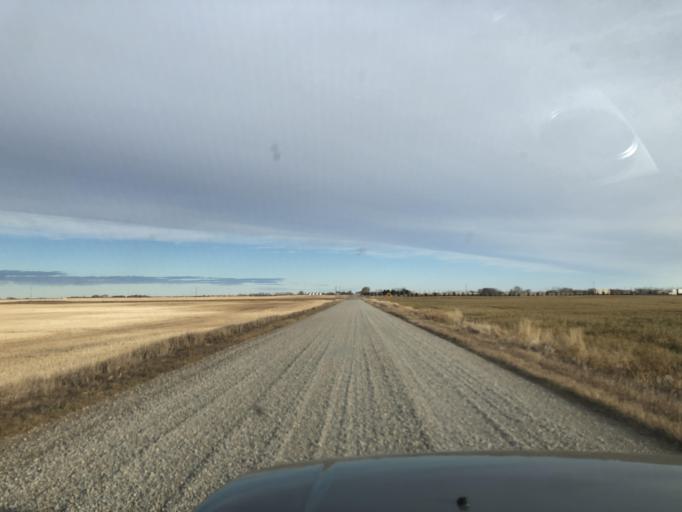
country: CA
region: Alberta
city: Strathmore
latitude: 50.8926
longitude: -113.5423
